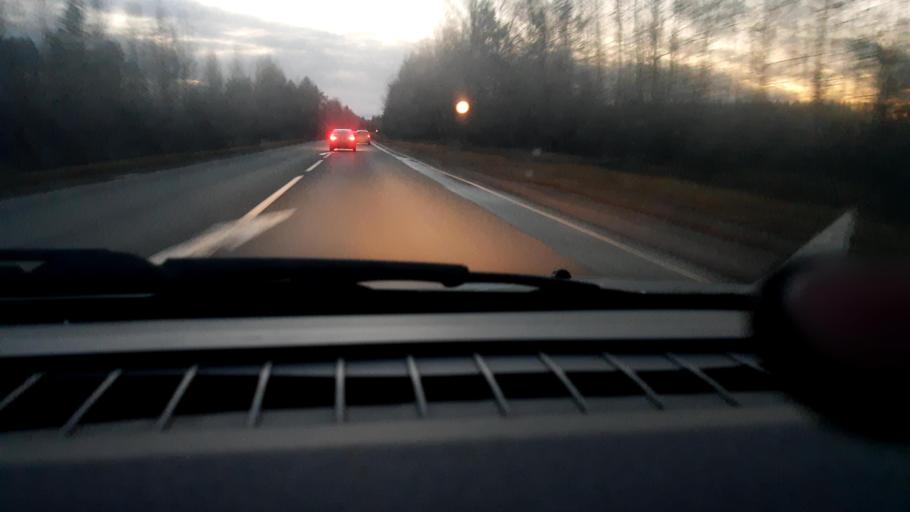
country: RU
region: Nizjnij Novgorod
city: Vladimirskoye
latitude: 56.8848
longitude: 44.9801
